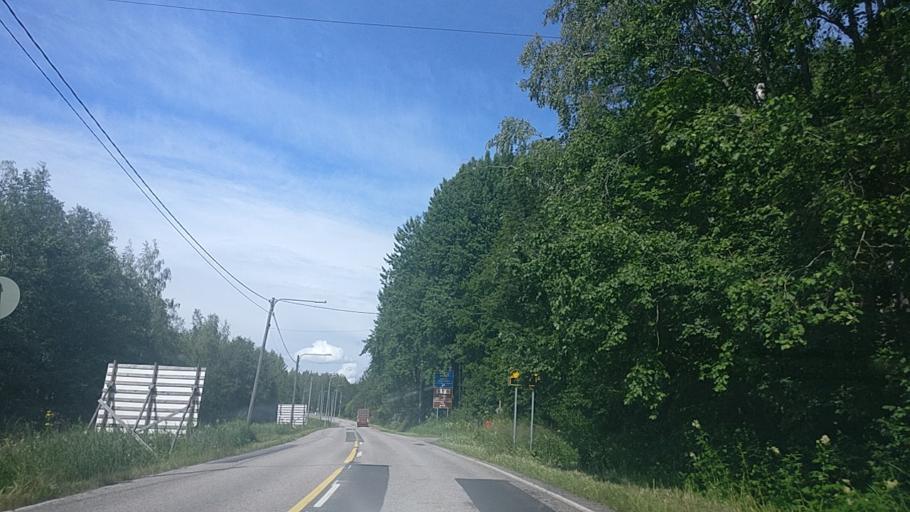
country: FI
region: Uusimaa
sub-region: Helsinki
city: Kauniainen
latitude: 60.3188
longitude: 24.7170
